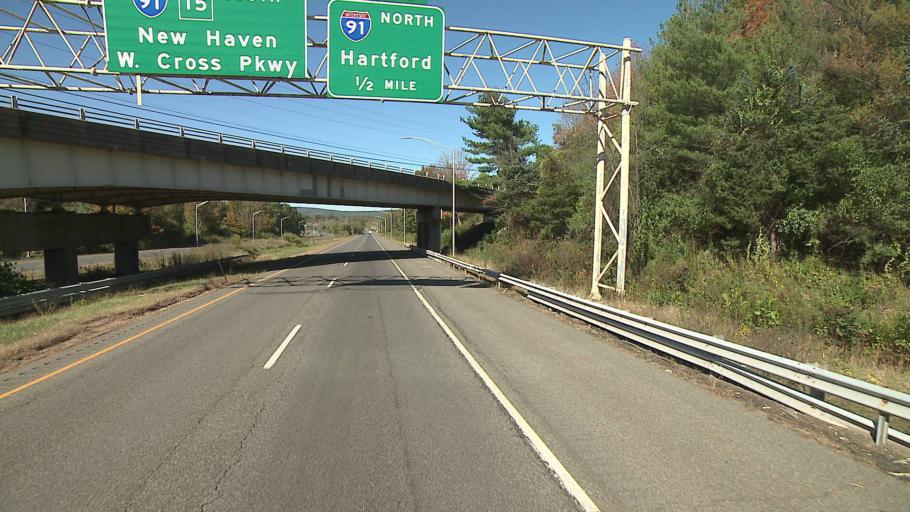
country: US
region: Connecticut
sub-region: New Haven County
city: Meriden
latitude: 41.5317
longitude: -72.7522
